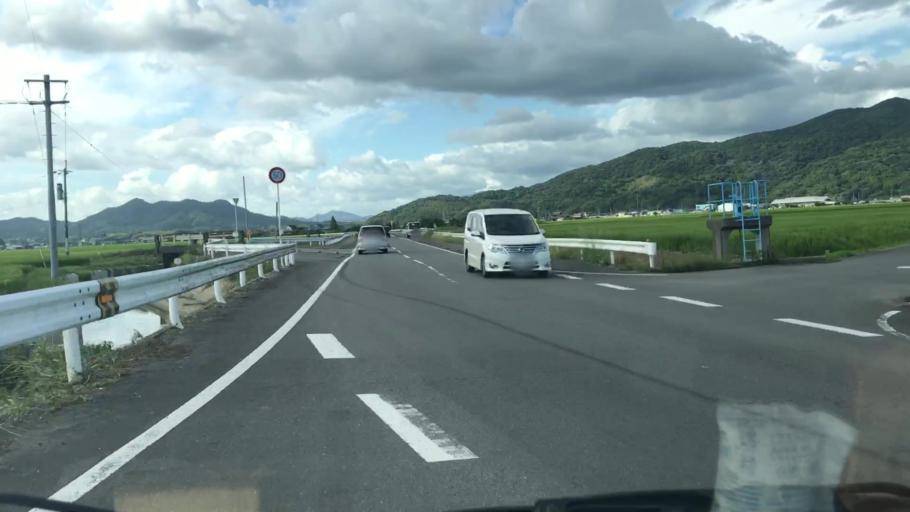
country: JP
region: Saga Prefecture
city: Kashima
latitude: 33.1138
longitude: 130.0816
